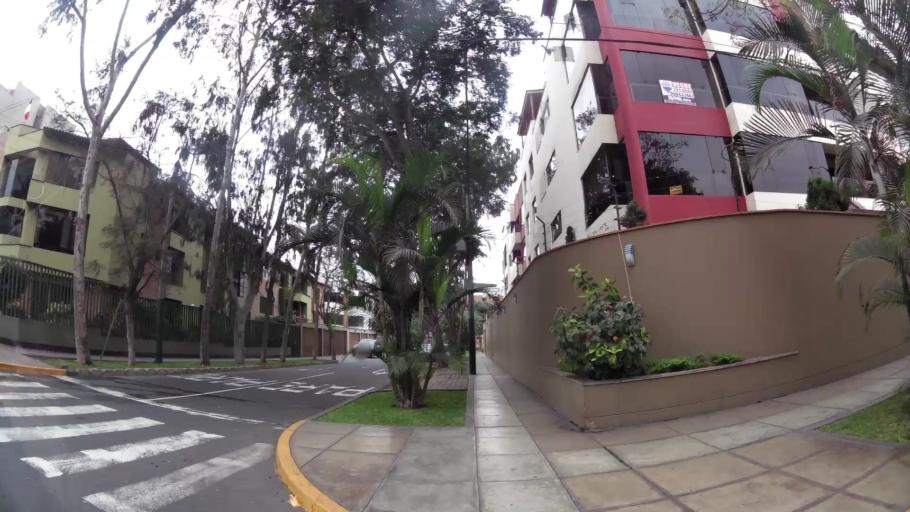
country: PE
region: Lima
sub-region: Lima
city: Surco
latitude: -12.1154
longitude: -76.9794
